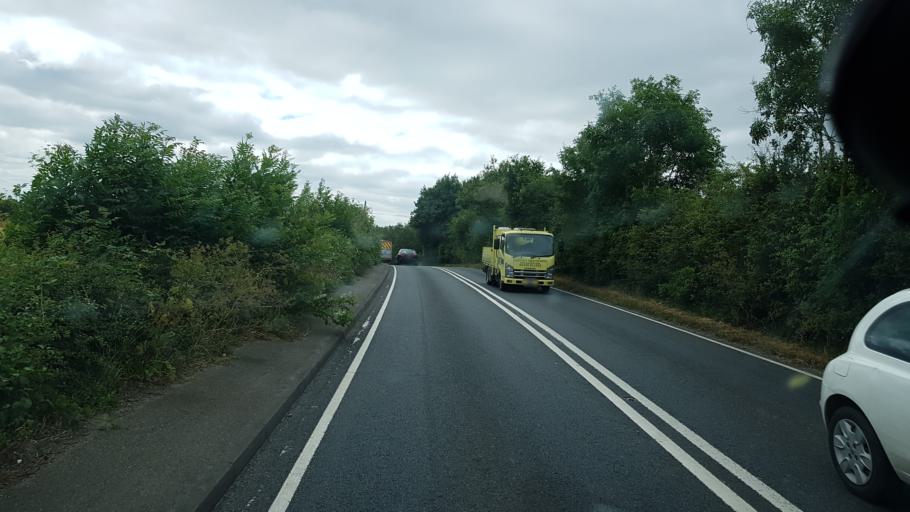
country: GB
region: England
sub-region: Surrey
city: Godstone
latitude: 51.2307
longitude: -0.0482
